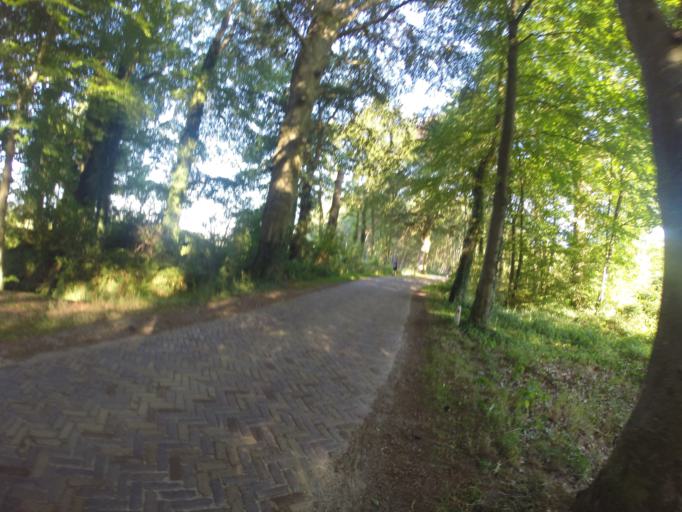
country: NL
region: Gelderland
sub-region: Gemeente Bronckhorst
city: Hengelo
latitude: 52.0928
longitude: 6.3684
